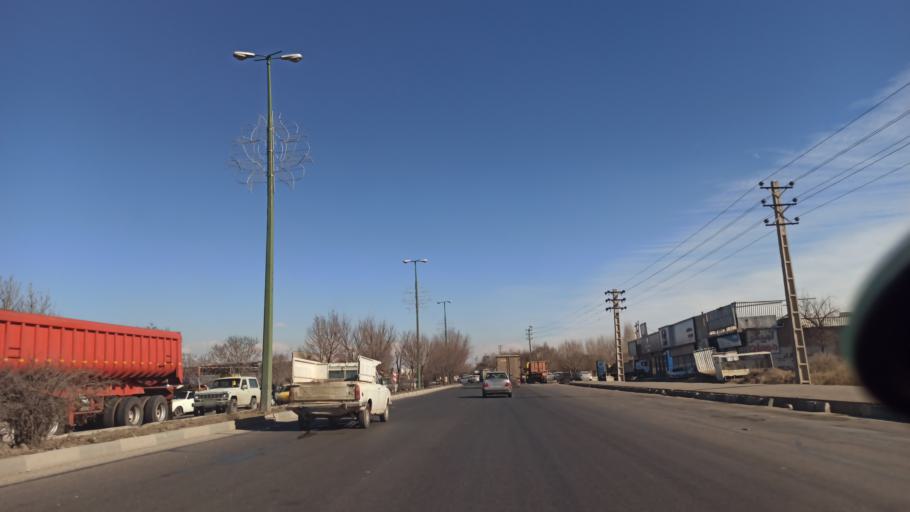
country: IR
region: Qazvin
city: Qazvin
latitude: 36.2566
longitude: 49.9824
